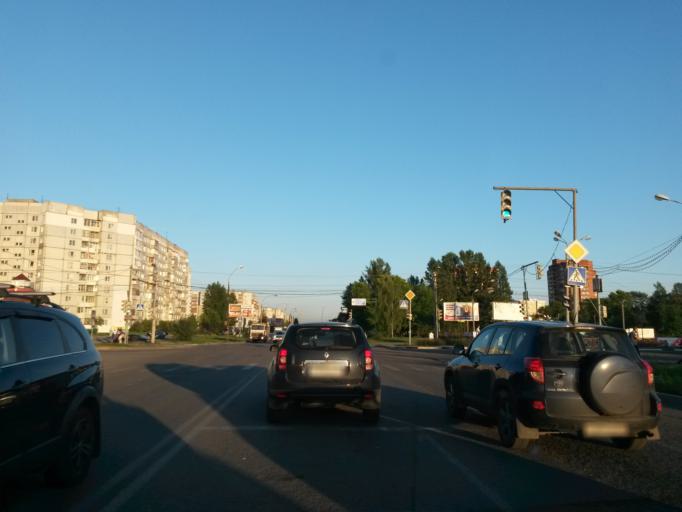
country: RU
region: Jaroslavl
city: Yaroslavl
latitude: 57.6981
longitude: 39.7637
